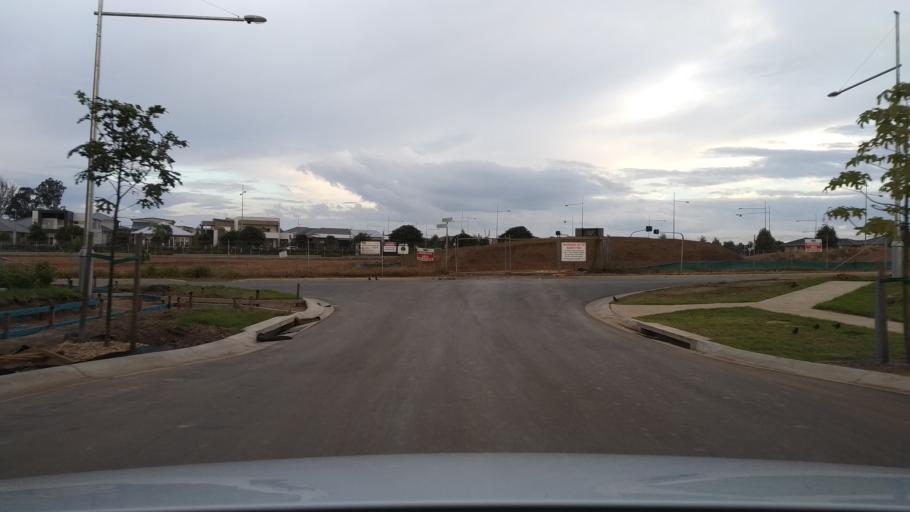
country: AU
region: New South Wales
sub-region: Camden
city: Narellan
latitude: -34.0003
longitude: 150.7356
